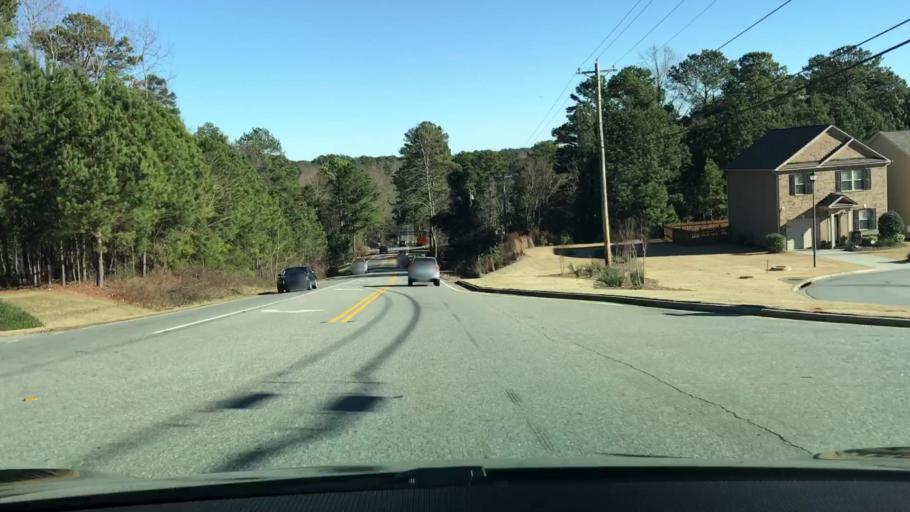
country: US
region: Georgia
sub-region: Forsyth County
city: Cumming
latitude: 34.1844
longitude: -84.1058
